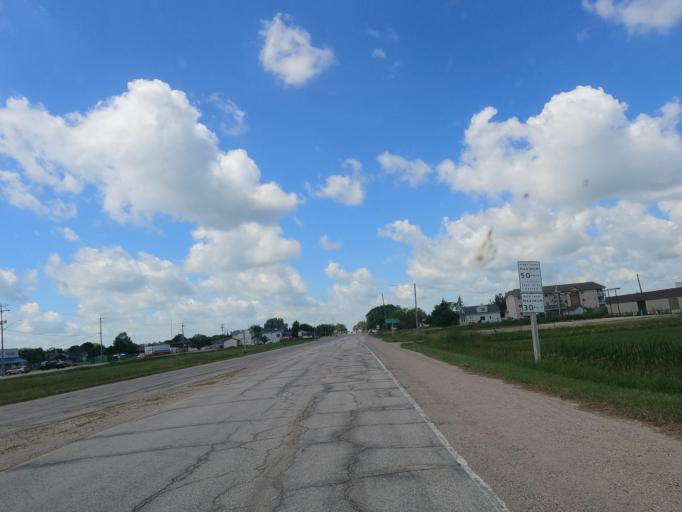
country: CA
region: Manitoba
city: Beausejour
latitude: 50.0618
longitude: -96.5013
